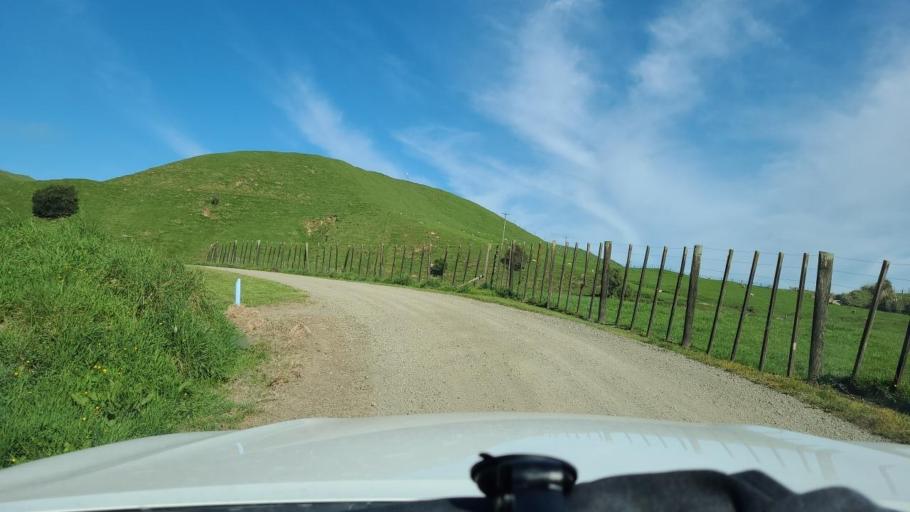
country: NZ
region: Bay of Plenty
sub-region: Opotiki District
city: Opotiki
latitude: -38.4615
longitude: 177.3818
